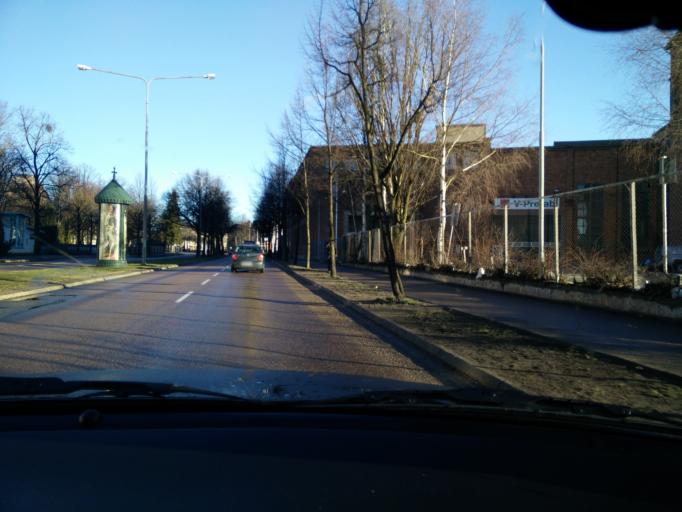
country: SE
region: Vaestmanland
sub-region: Vasteras
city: Vasteras
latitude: 59.6130
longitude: 16.5565
